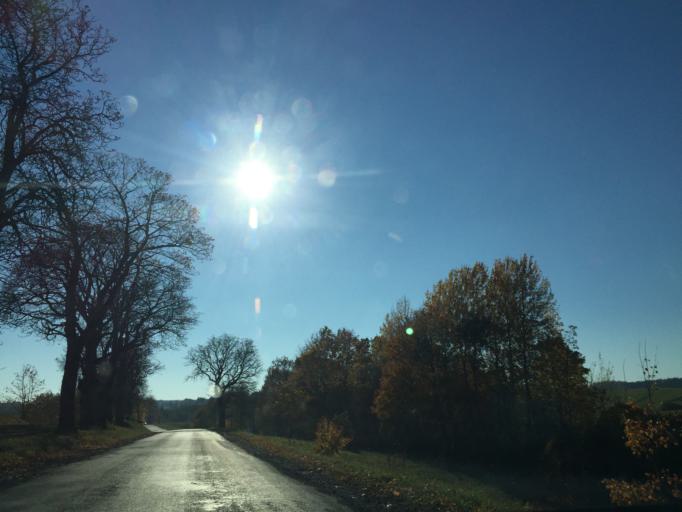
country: LT
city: Plateliai
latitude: 56.0372
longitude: 21.8132
